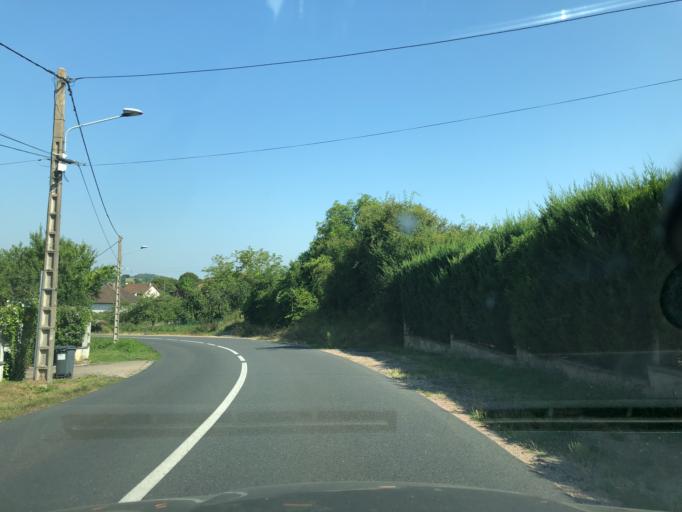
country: FR
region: Auvergne
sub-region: Departement de l'Allier
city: Cusset
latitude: 46.1307
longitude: 3.4757
